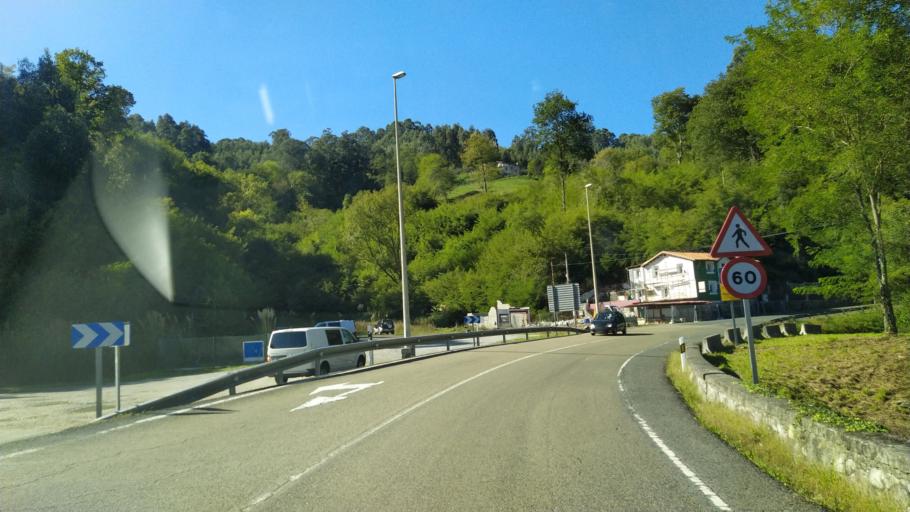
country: ES
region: Cantabria
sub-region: Provincia de Cantabria
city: Liendo
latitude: 43.3792
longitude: -3.3223
